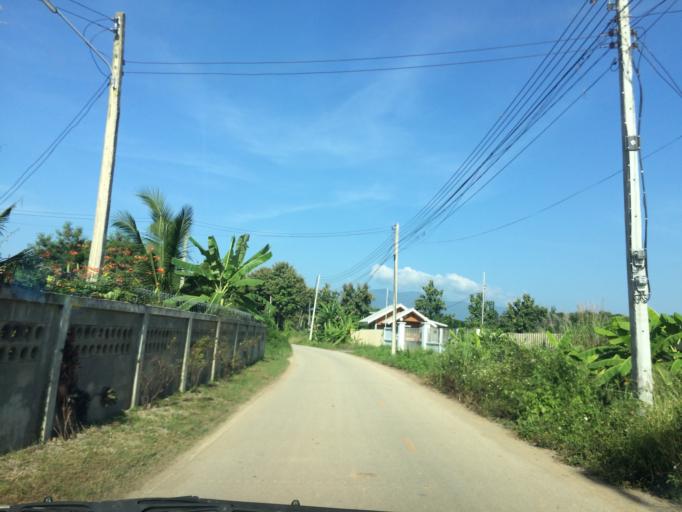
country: TH
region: Chiang Mai
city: Saraphi
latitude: 18.7282
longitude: 99.0122
